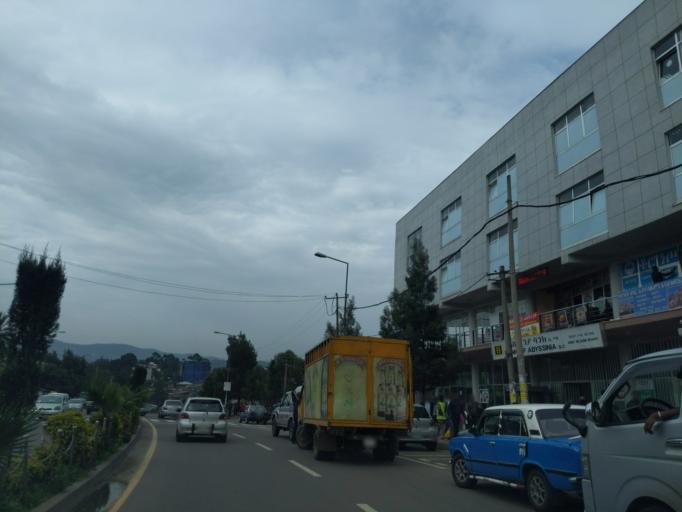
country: ET
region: Adis Abeba
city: Addis Ababa
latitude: 9.0323
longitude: 38.7659
